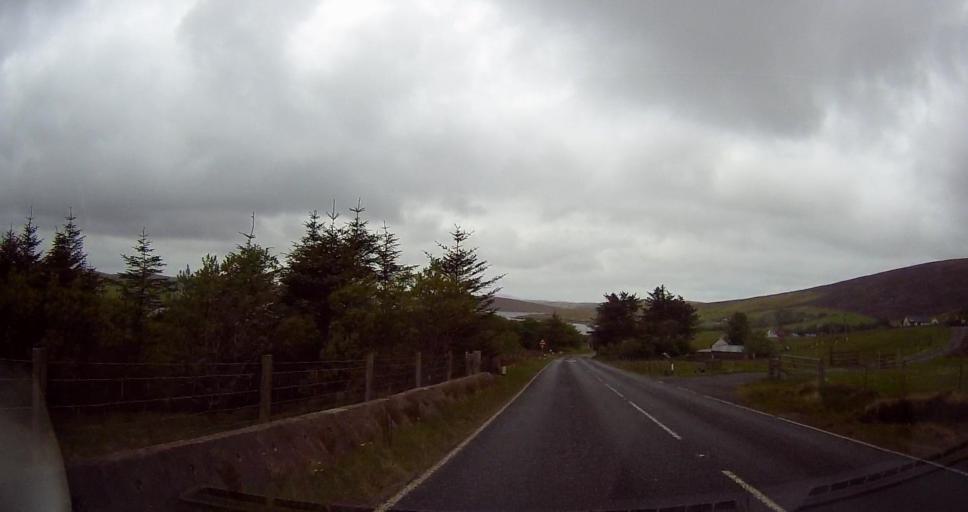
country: GB
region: Scotland
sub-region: Shetland Islands
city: Lerwick
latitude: 60.2413
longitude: -1.3409
